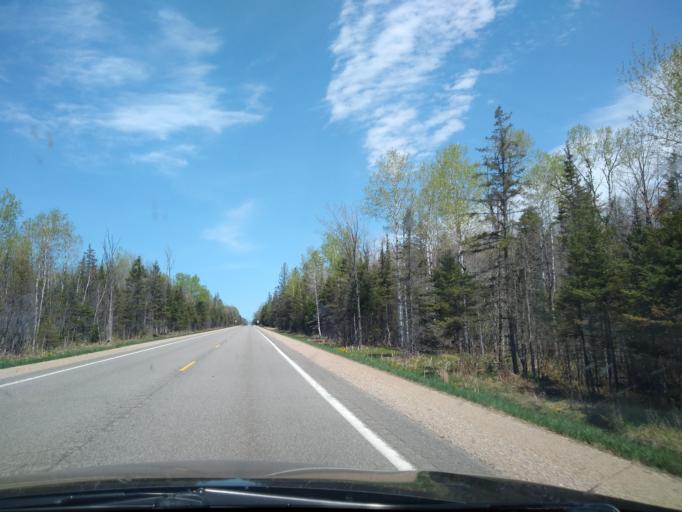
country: US
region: Michigan
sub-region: Delta County
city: Gladstone
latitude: 46.0467
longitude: -86.9814
